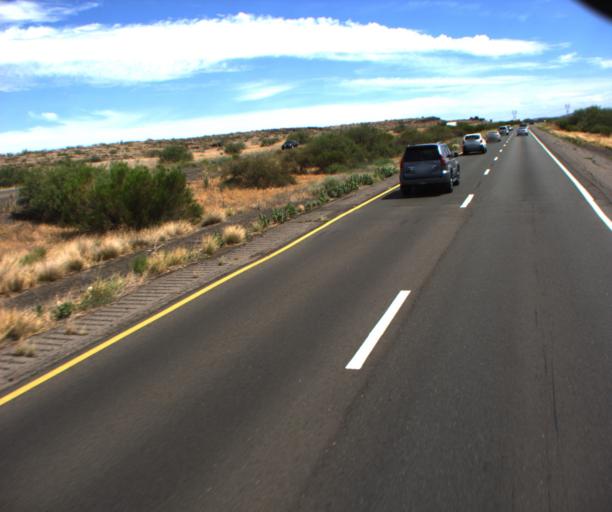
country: US
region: Arizona
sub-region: Yavapai County
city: Spring Valley
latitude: 34.3703
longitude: -112.1108
